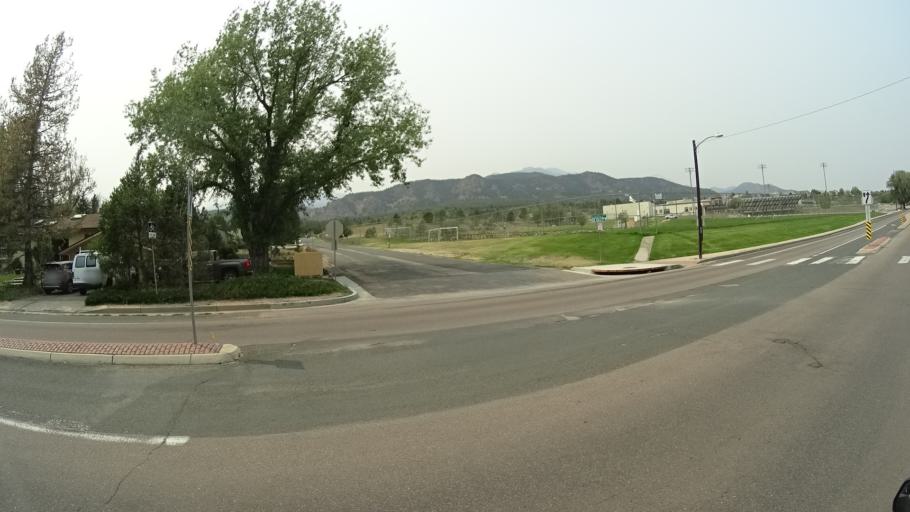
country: US
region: Colorado
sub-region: El Paso County
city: Colorado Springs
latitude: 38.8020
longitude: -104.8534
